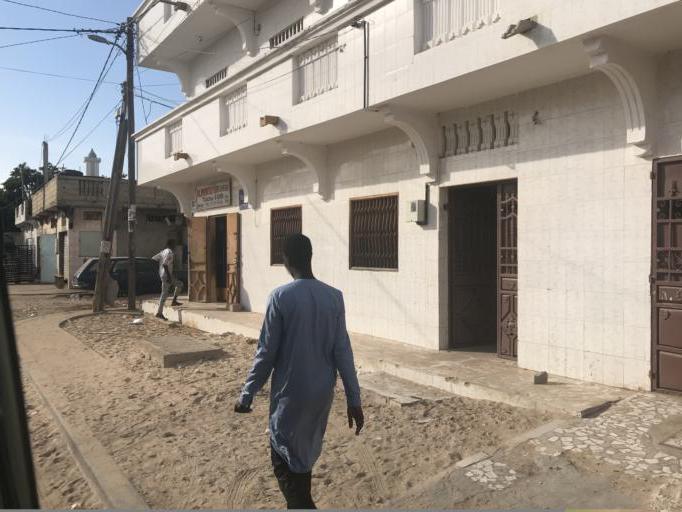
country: SN
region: Saint-Louis
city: Saint-Louis
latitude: 15.9934
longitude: -16.4904
